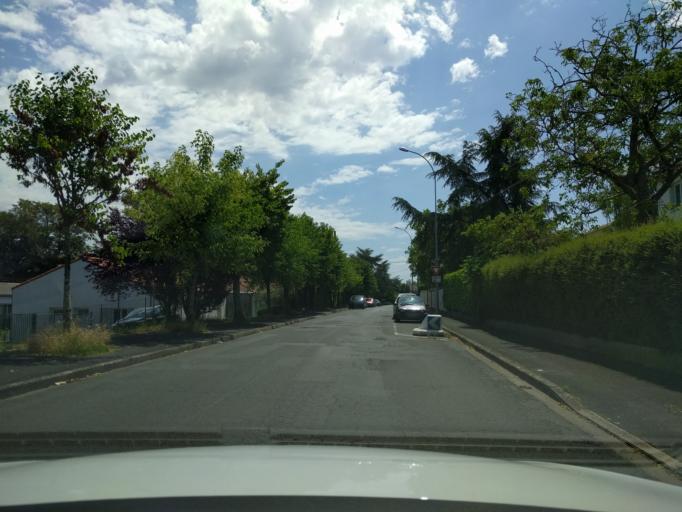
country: FR
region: Poitou-Charentes
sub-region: Departement des Deux-Sevres
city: Niort
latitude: 46.3421
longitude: -0.4800
